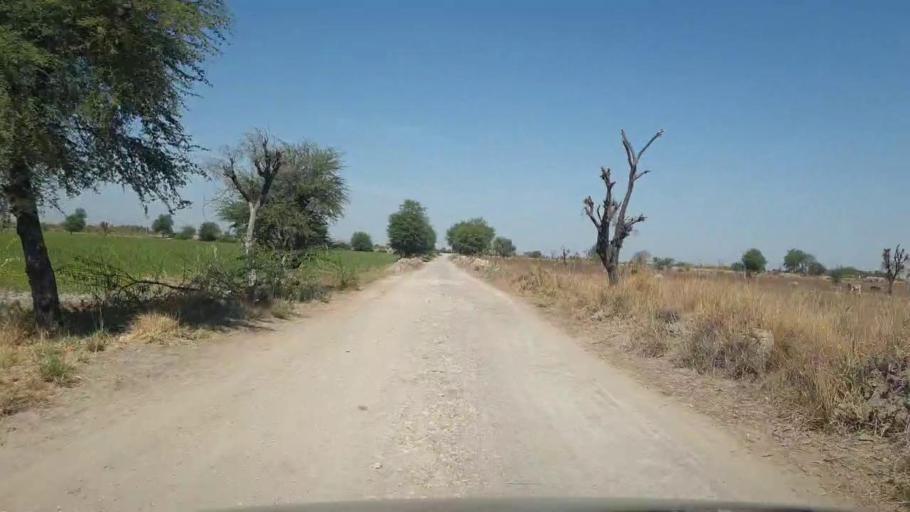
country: PK
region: Sindh
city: Dhoro Naro
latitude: 25.4550
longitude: 69.6084
